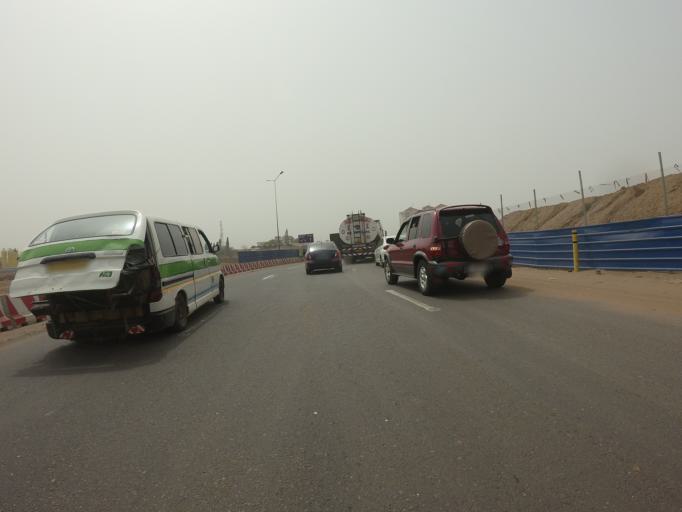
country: GH
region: Greater Accra
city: Tema
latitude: 5.6865
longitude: -0.0152
